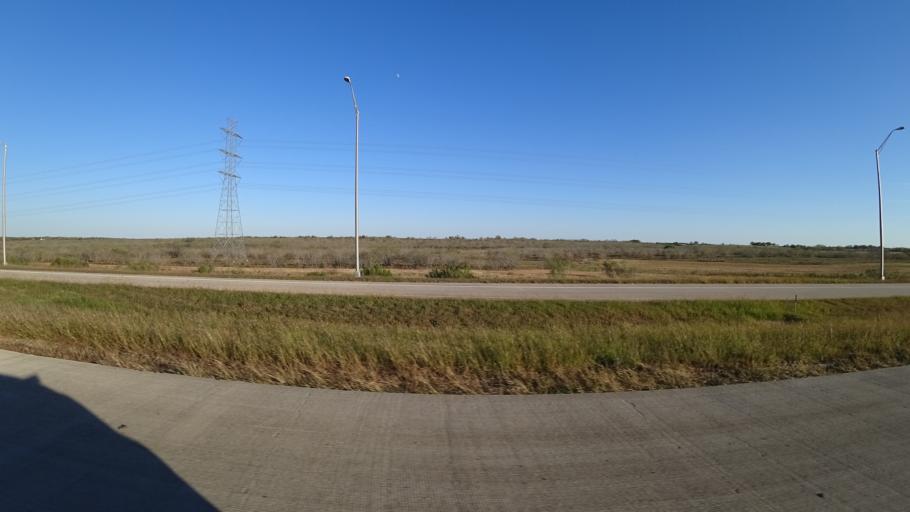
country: US
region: Texas
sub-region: Travis County
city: Onion Creek
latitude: 30.1093
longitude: -97.6644
